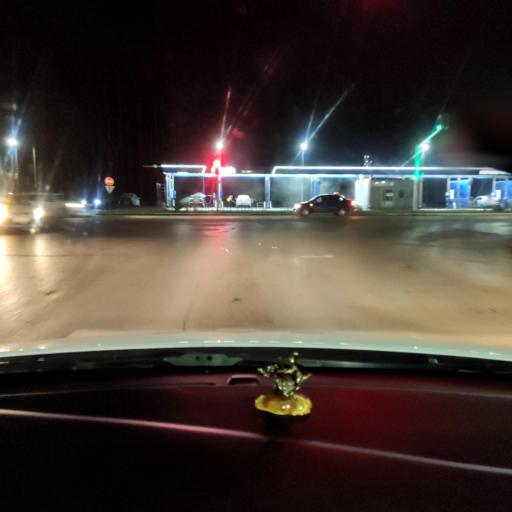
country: RU
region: Tatarstan
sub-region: Zelenodol'skiy Rayon
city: Zelenodolsk
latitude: 55.8517
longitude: 48.5669
